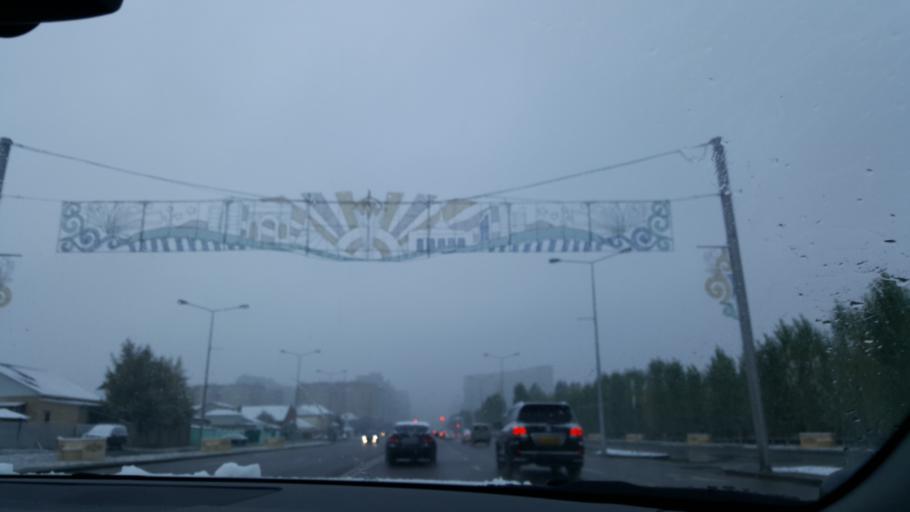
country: KZ
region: Astana Qalasy
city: Astana
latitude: 51.1438
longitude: 71.4915
